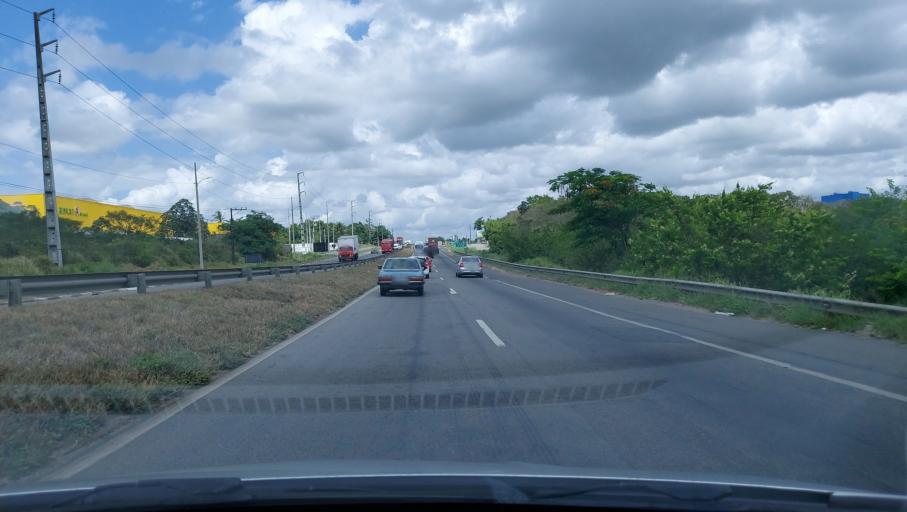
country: BR
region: Bahia
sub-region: Conceicao Do Jacuipe
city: Conceicao do Jacuipe
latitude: -12.3362
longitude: -38.8510
